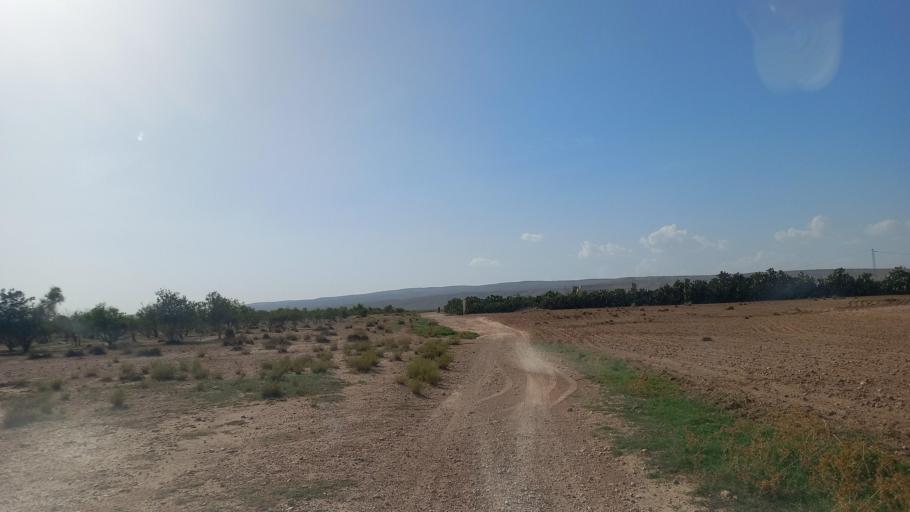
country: TN
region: Al Qasrayn
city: Kasserine
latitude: 35.3136
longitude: 9.0124
